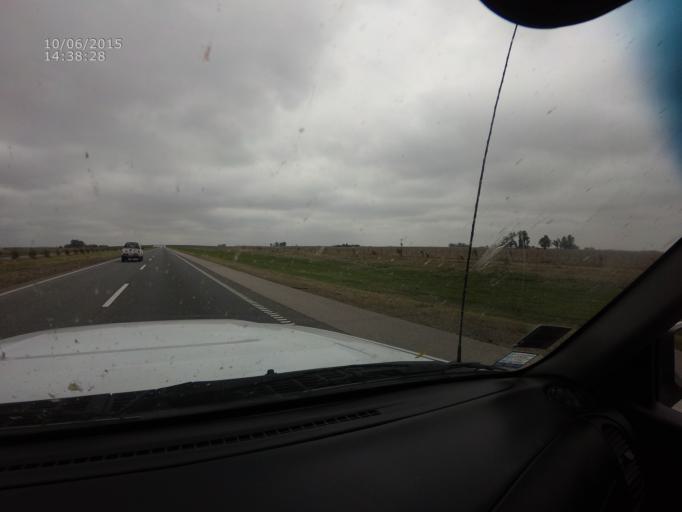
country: AR
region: Cordoba
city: James Craik
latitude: -32.0919
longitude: -63.4745
